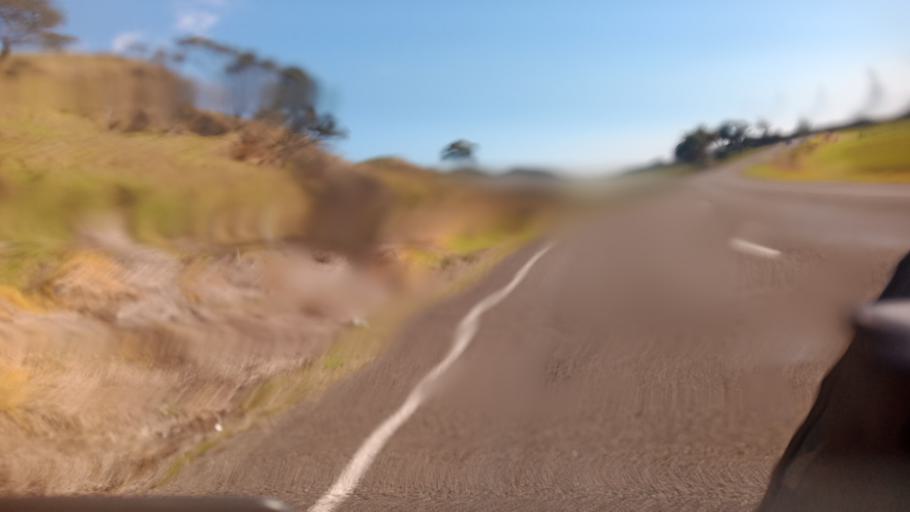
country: NZ
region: Bay of Plenty
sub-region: Opotiki District
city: Opotiki
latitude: -37.9919
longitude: 177.3189
